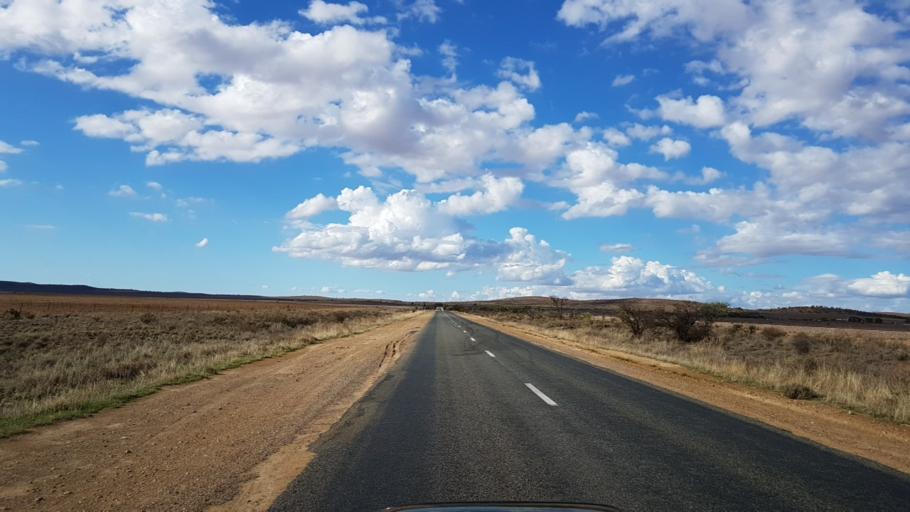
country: AU
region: South Australia
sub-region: Peterborough
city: Peterborough
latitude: -32.9666
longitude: 138.8744
